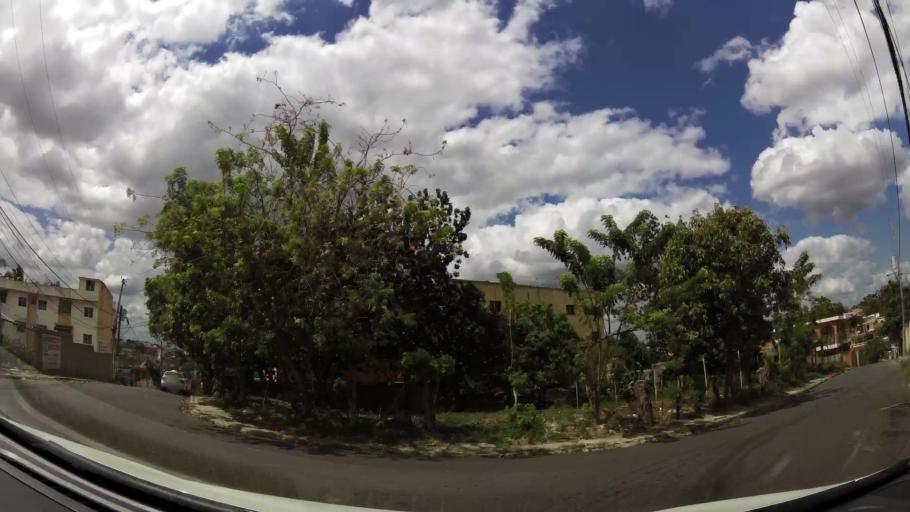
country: DO
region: Nacional
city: Ensanche Luperon
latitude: 18.5238
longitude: -69.9120
